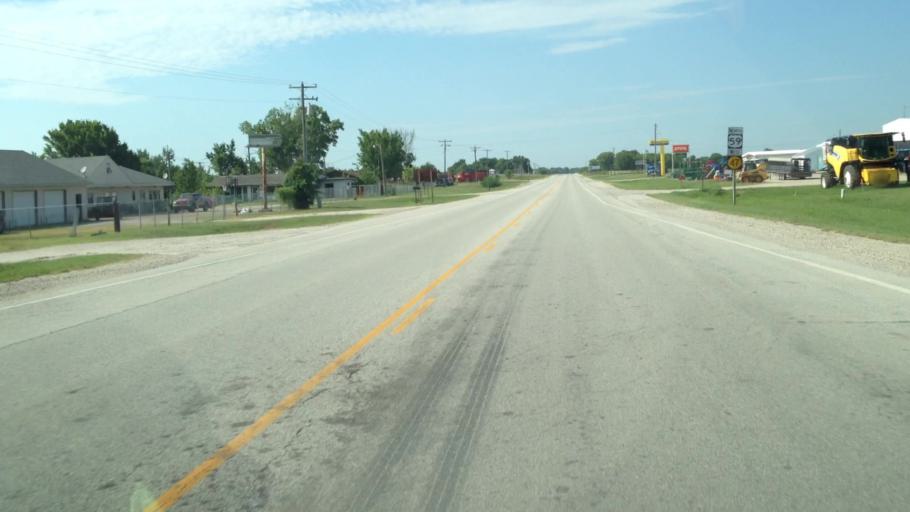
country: US
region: Kansas
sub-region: Neosho County
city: Erie
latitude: 37.5160
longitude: -95.2699
